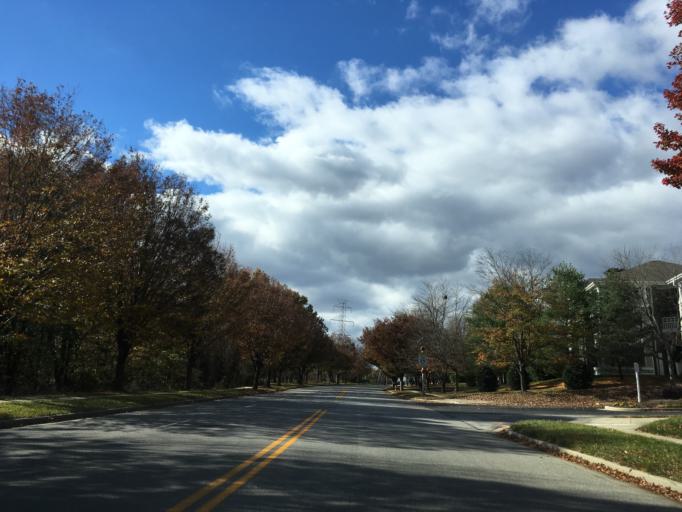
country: US
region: Maryland
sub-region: Howard County
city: Columbia
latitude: 39.2075
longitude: -76.8096
